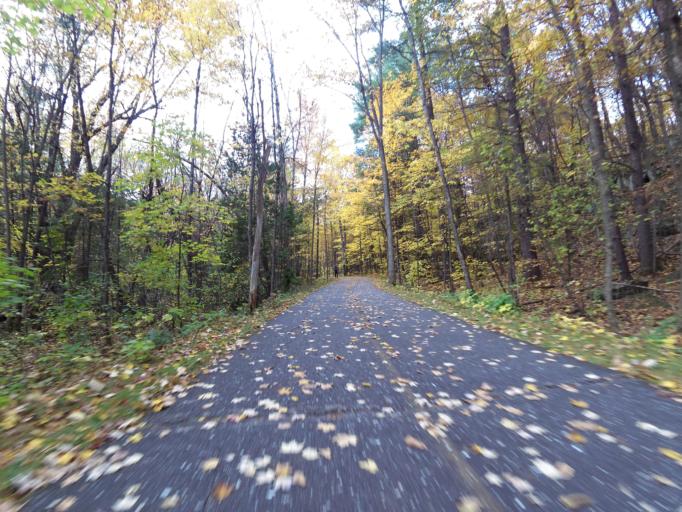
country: CA
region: Quebec
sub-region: Outaouais
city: Gatineau
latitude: 45.4515
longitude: -75.7699
